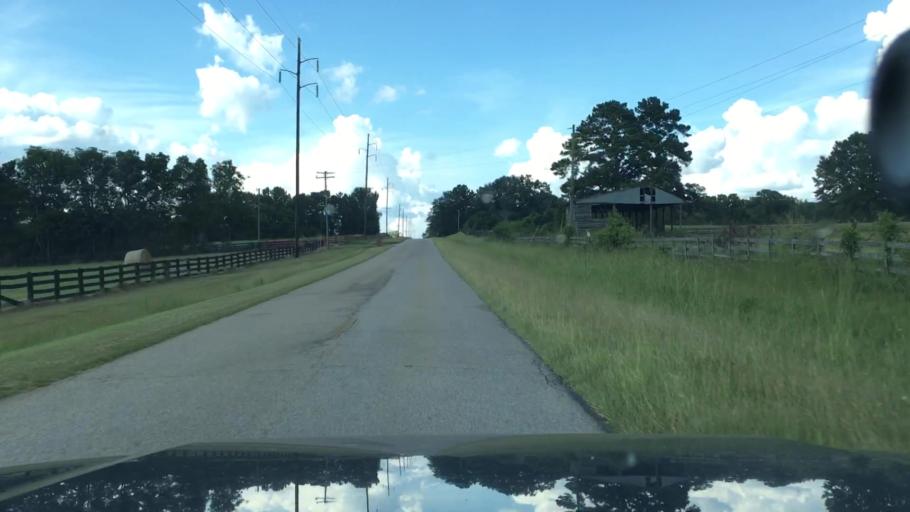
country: US
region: Georgia
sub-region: Monroe County
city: Forsyth
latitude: 32.9940
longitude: -83.8791
